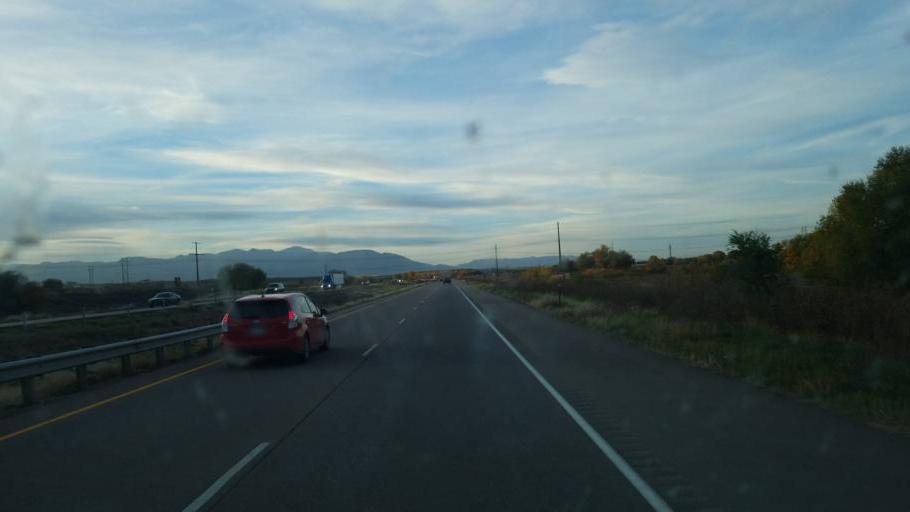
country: US
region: Colorado
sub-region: El Paso County
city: Fountain
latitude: 38.5770
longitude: -104.6614
